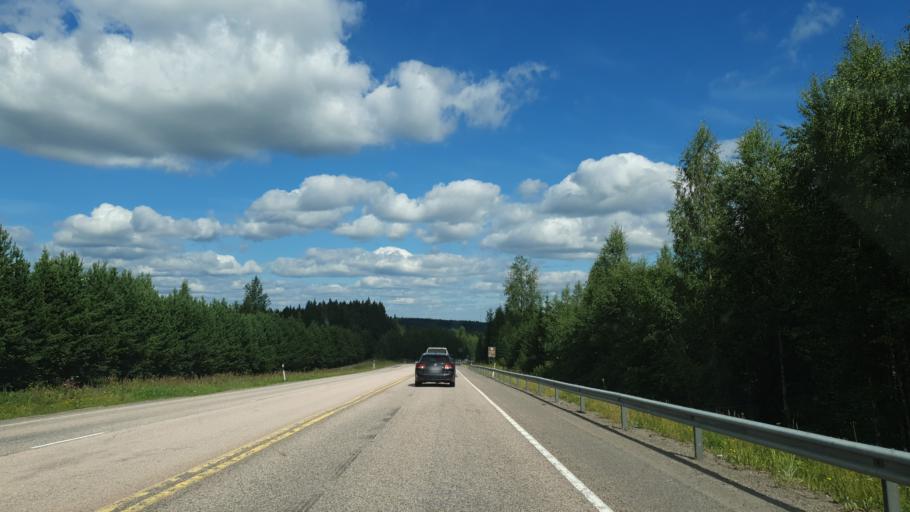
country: FI
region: Central Finland
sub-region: Jaemsae
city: Jaemsae
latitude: 61.8300
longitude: 25.0858
